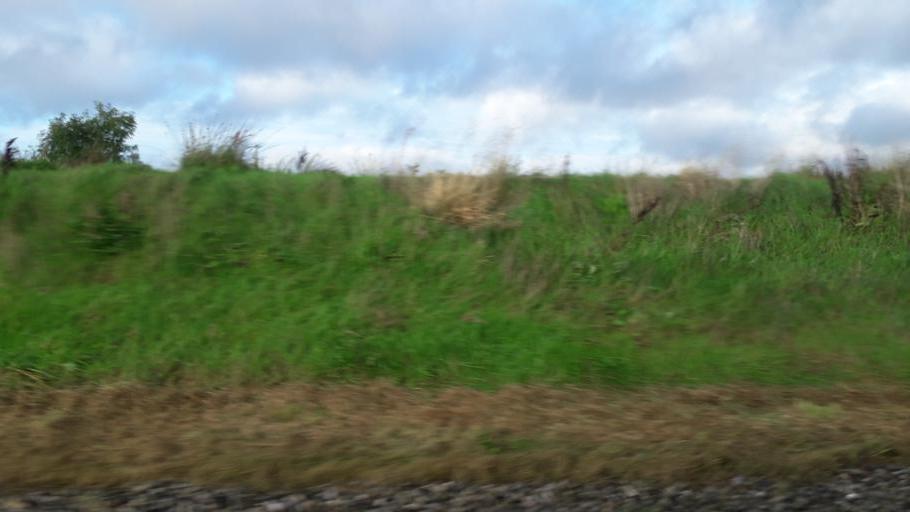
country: IE
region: Connaught
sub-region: Roscommon
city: Ballaghaderreen
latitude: 53.8938
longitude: -8.5131
